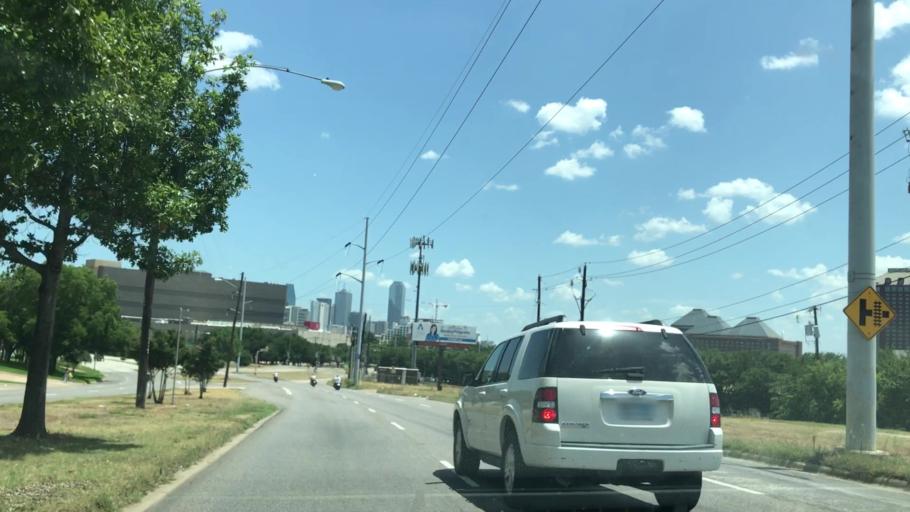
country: US
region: Texas
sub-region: Dallas County
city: Dallas
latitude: 32.8072
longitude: -96.8317
